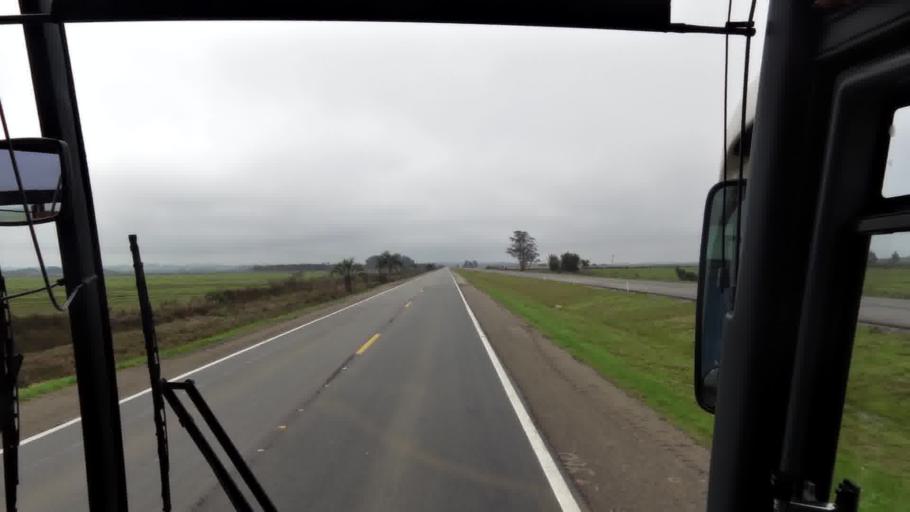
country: BR
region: Rio Grande do Sul
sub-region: Pelotas
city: Pelotas
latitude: -31.5914
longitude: -52.2829
